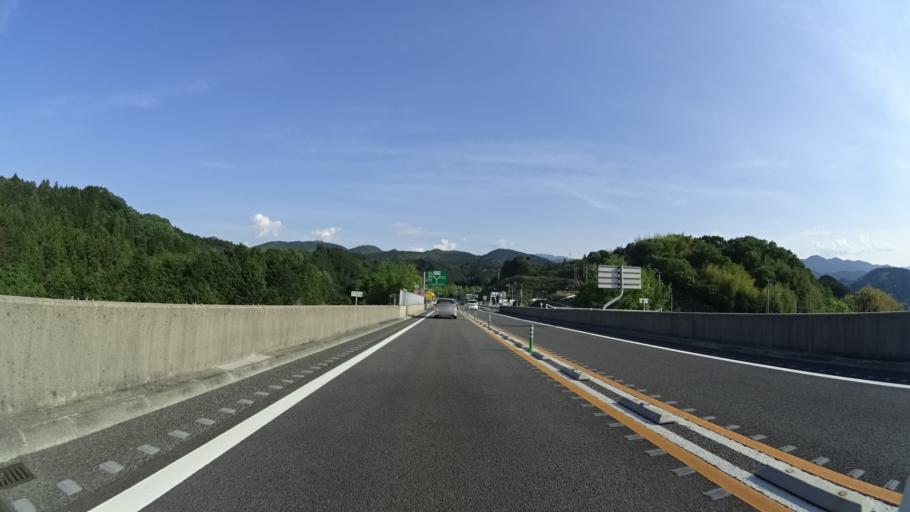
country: JP
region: Ehime
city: Saijo
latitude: 33.8877
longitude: 133.0870
